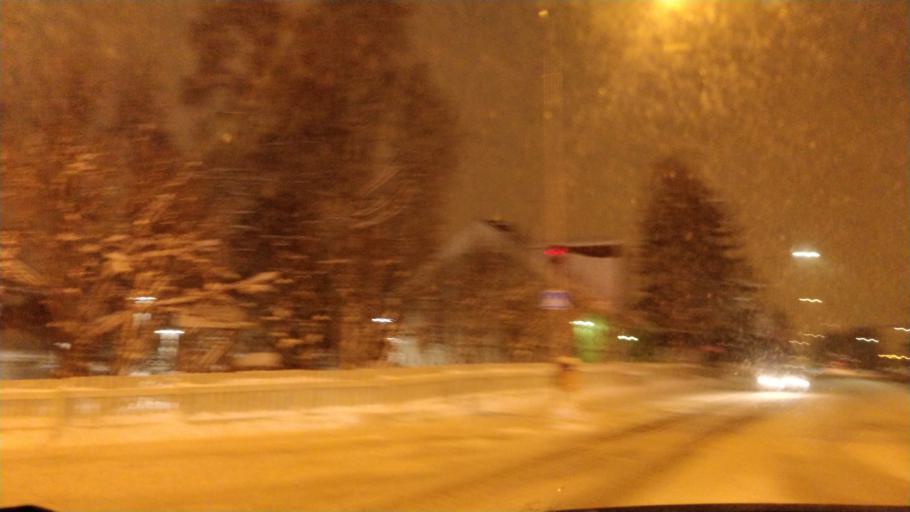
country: FI
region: Lapland
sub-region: Rovaniemi
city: Rovaniemi
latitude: 66.5022
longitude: 25.7243
